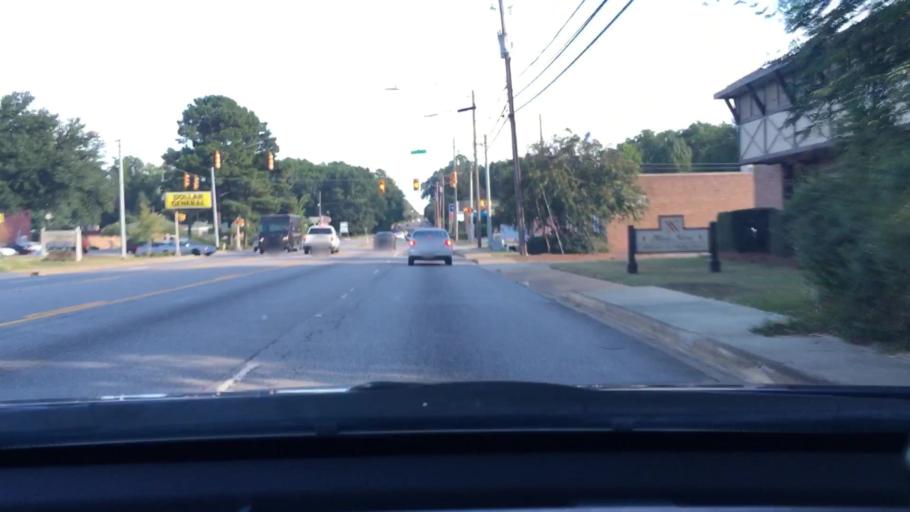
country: US
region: South Carolina
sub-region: Sumter County
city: Sumter
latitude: 33.9309
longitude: -80.3680
